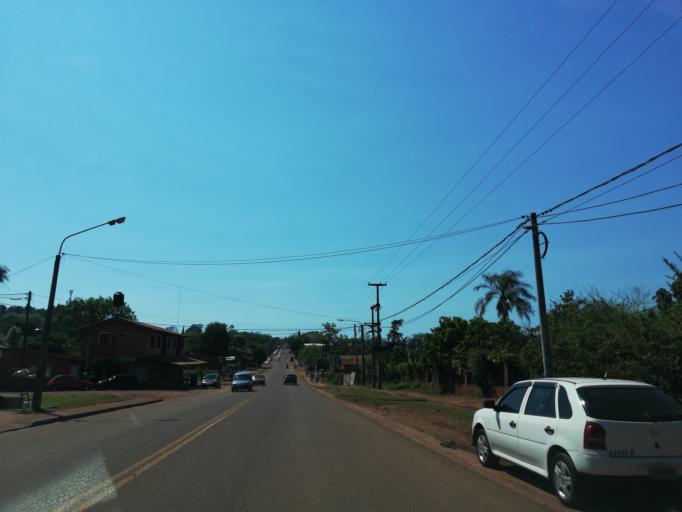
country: AR
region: Misiones
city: Puerto Eldorado
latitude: -26.4068
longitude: -54.6624
